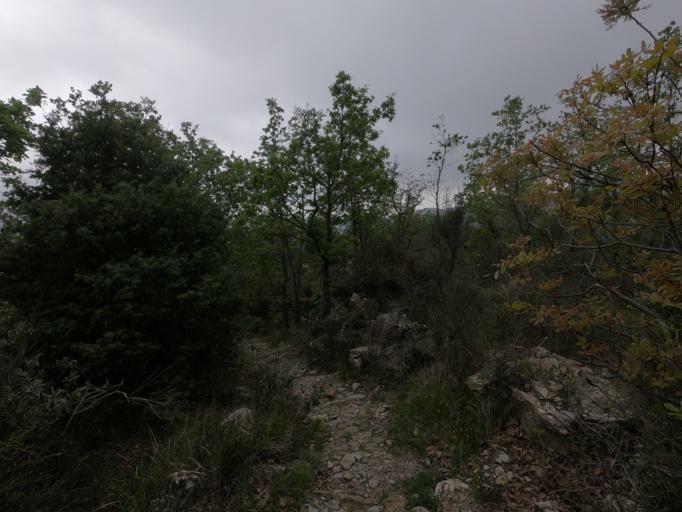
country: IT
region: Liguria
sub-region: Provincia di Imperia
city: Villa Faraldi
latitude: 43.9706
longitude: 8.0895
